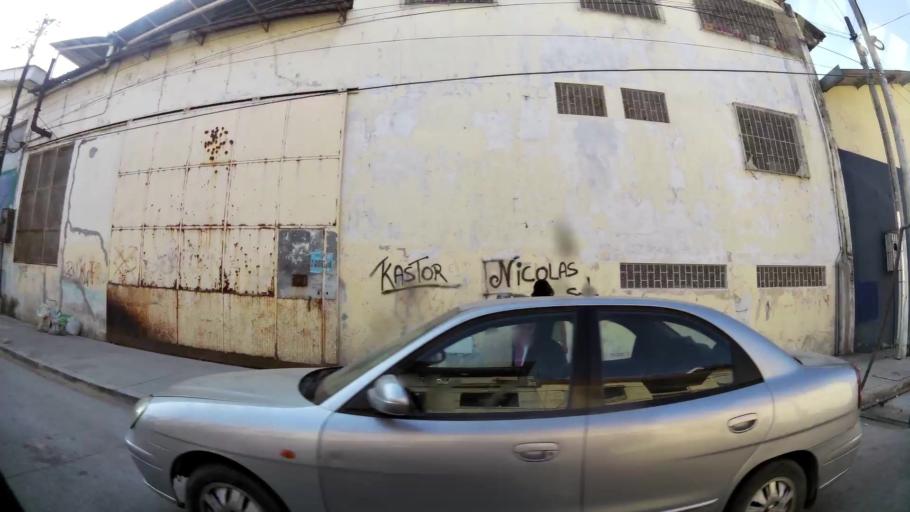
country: EC
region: Guayas
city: Guayaquil
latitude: -2.1559
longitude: -79.9256
